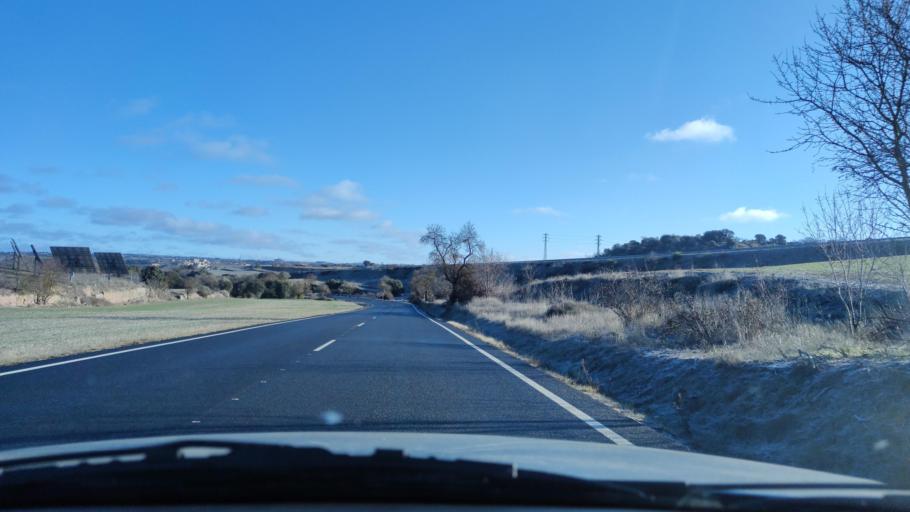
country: ES
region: Catalonia
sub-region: Provincia de Lleida
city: Cervera
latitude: 41.6849
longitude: 1.3012
